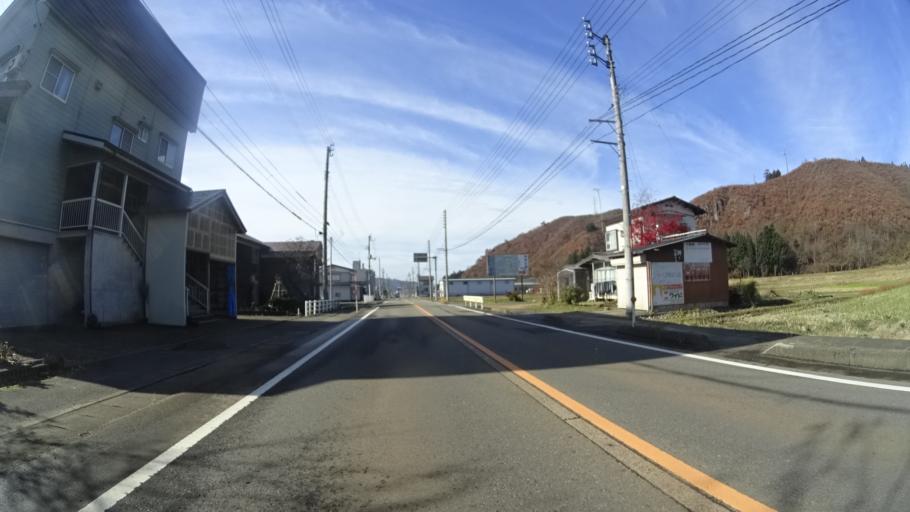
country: JP
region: Niigata
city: Muikamachi
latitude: 37.2271
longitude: 138.9994
